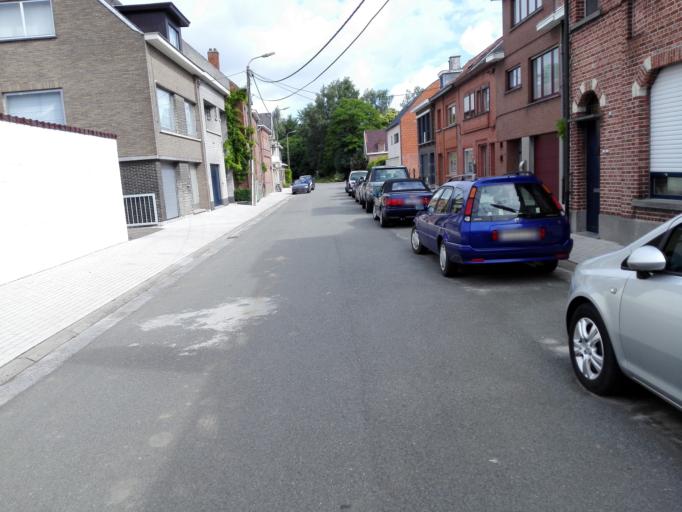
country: BE
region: Flanders
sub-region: Provincie Oost-Vlaanderen
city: Dendermonde
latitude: 51.0226
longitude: 4.0932
